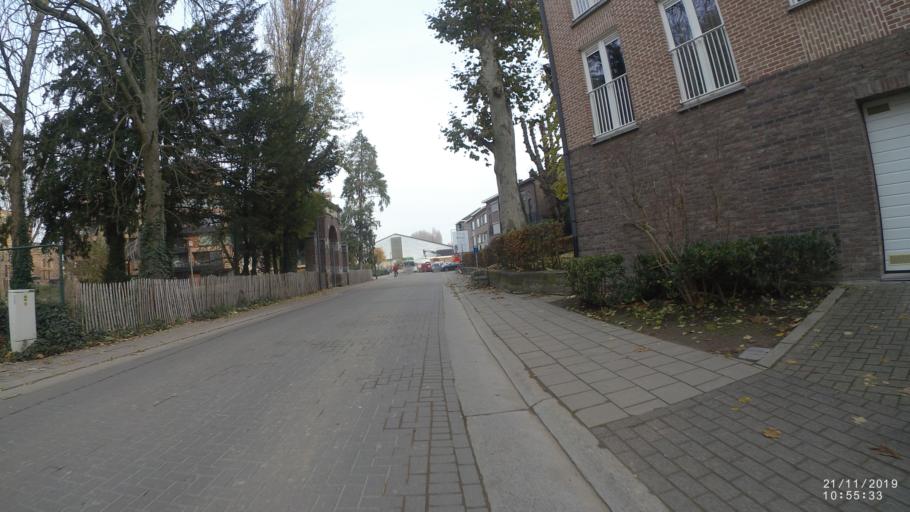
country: BE
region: Flanders
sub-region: Provincie Limburg
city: Sint-Truiden
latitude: 50.8194
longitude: 5.1885
